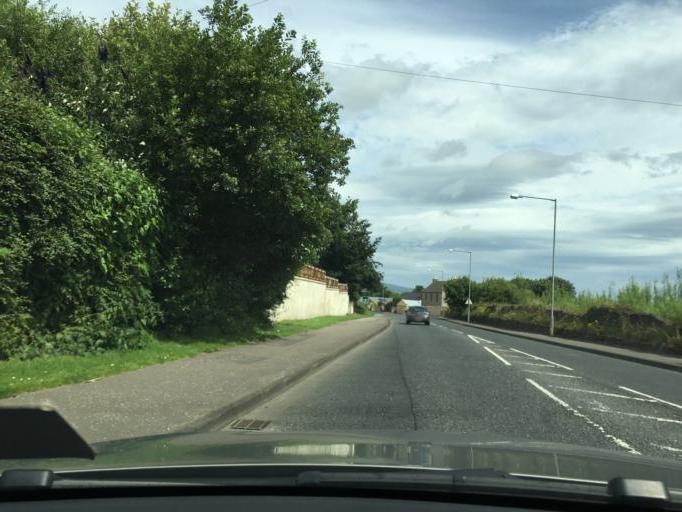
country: GB
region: Northern Ireland
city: Culmore
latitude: 55.0433
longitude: -7.2749
